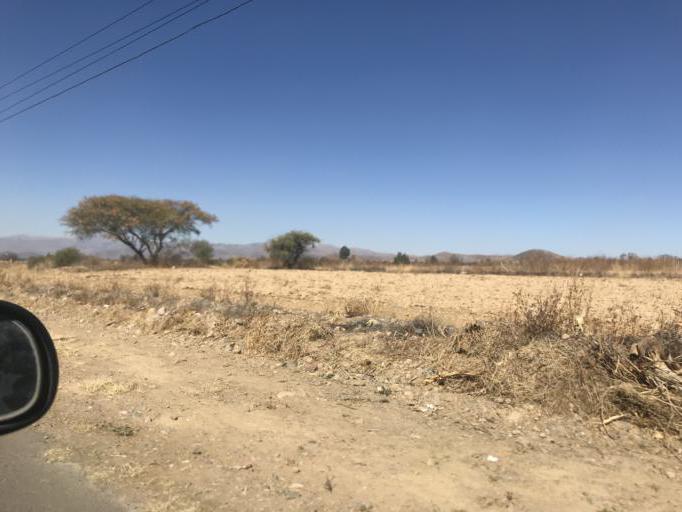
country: BO
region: Cochabamba
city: Tarata
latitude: -17.6039
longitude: -65.9891
